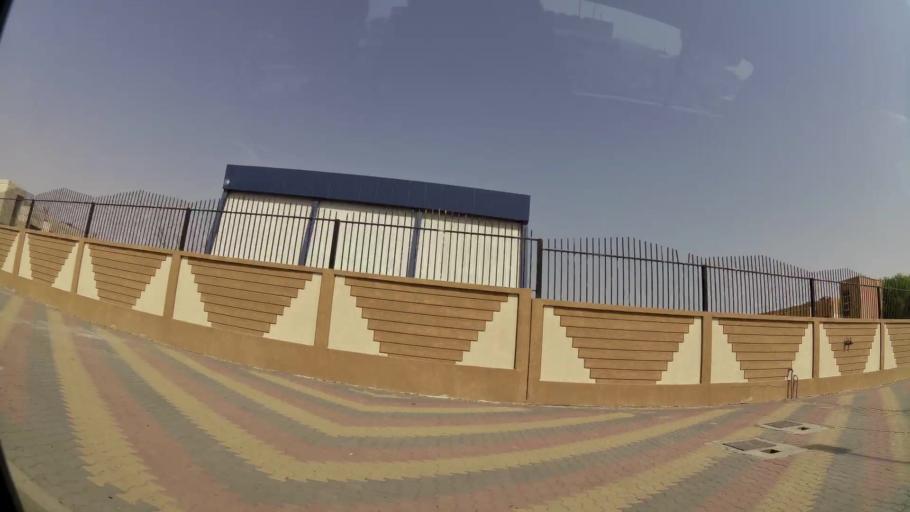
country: KW
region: Muhafazat al Jahra'
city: Al Jahra'
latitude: 29.3366
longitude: 47.6961
